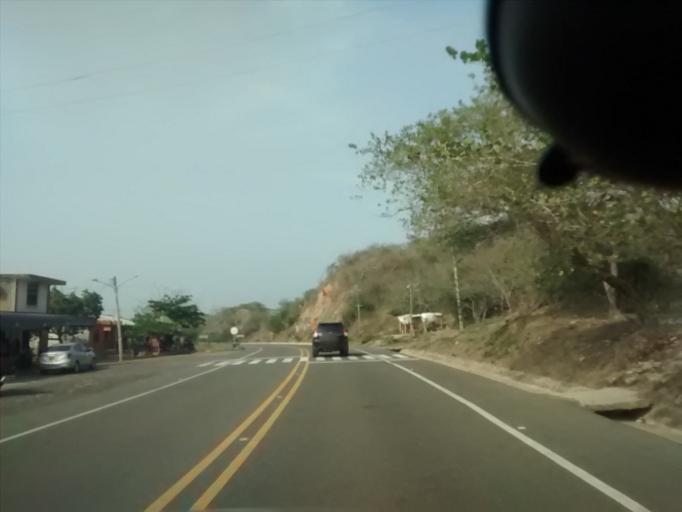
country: CO
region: Bolivar
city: Clemencia
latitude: 10.6396
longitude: -75.4062
